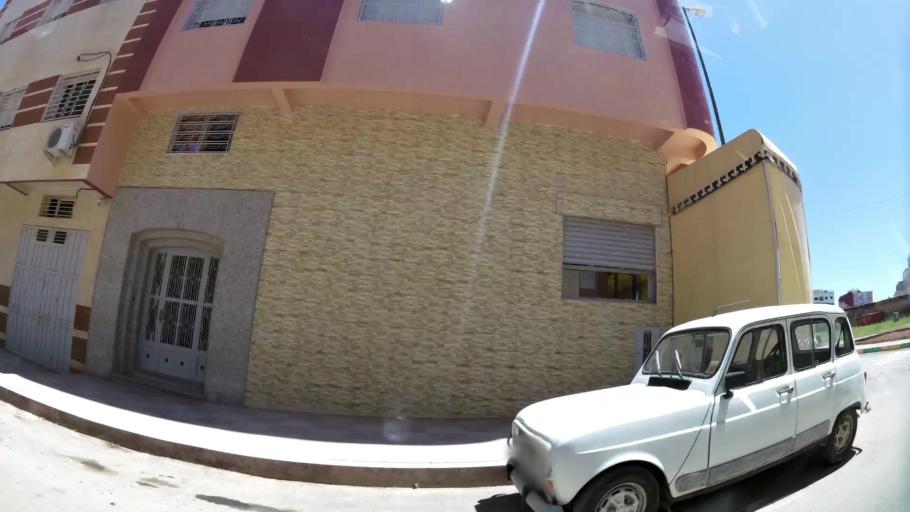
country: MA
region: Meknes-Tafilalet
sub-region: Meknes
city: Meknes
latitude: 33.8645
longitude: -5.5755
